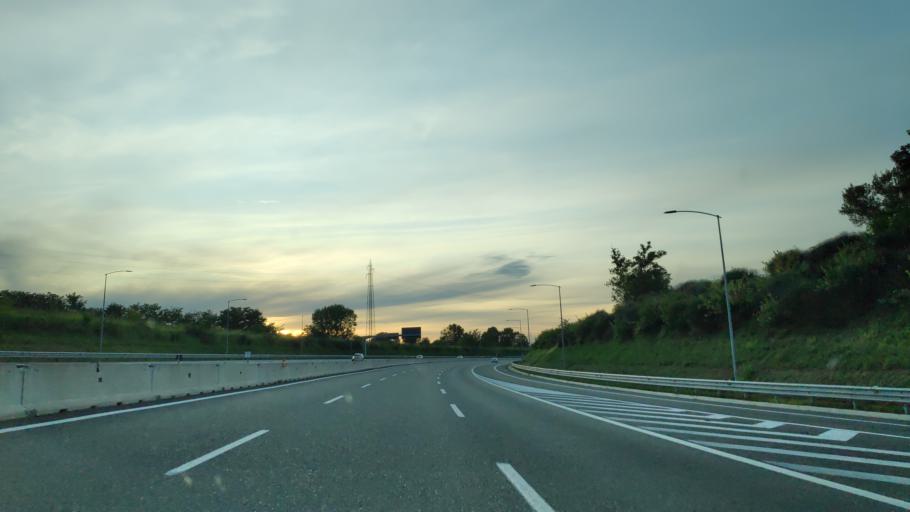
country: IT
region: Lombardy
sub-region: Citta metropolitana di Milano
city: Gorgonzola
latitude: 45.5480
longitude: 9.4151
